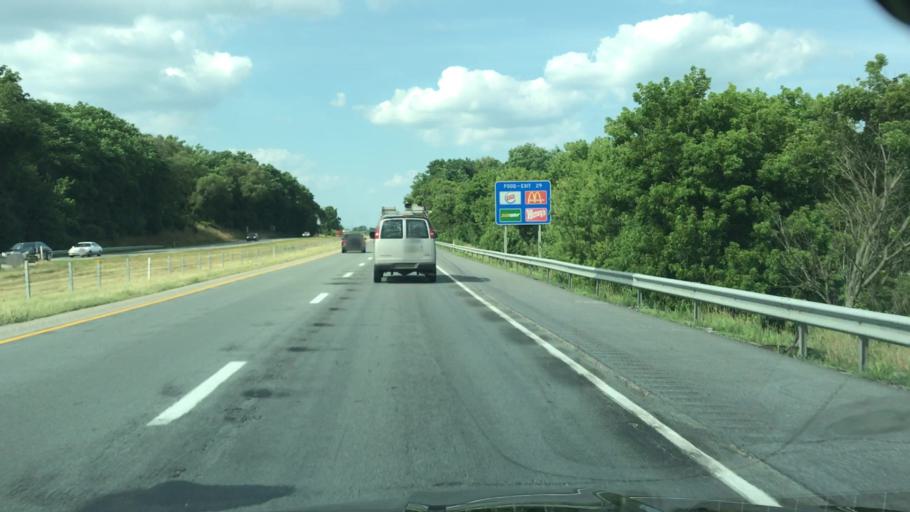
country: US
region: Pennsylvania
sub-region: Cumberland County
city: Shippensburg
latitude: 40.0519
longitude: -77.4854
